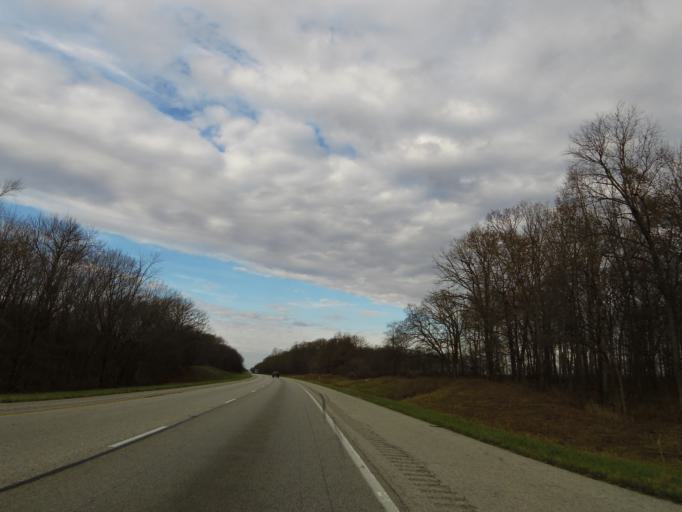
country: US
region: Illinois
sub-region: Washington County
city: Nashville
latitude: 38.4081
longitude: -89.4117
